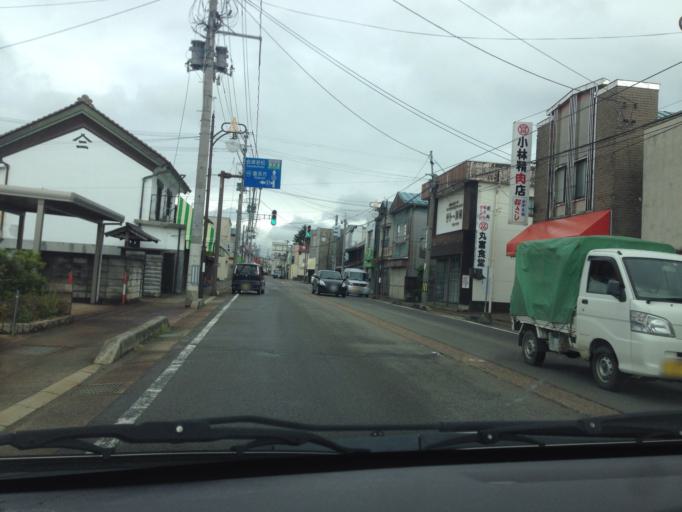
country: JP
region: Fukushima
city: Kitakata
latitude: 37.5610
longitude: 139.8249
